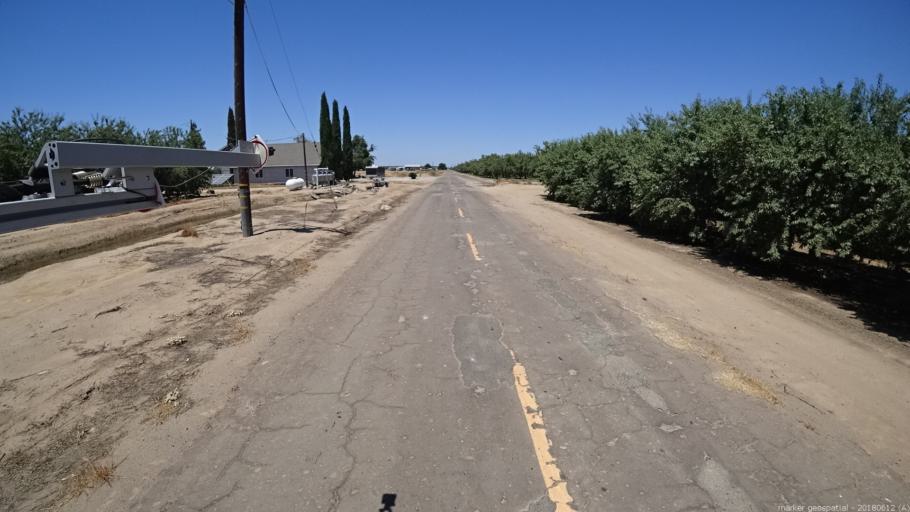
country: US
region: California
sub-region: Madera County
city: Chowchilla
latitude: 37.0652
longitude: -120.2659
